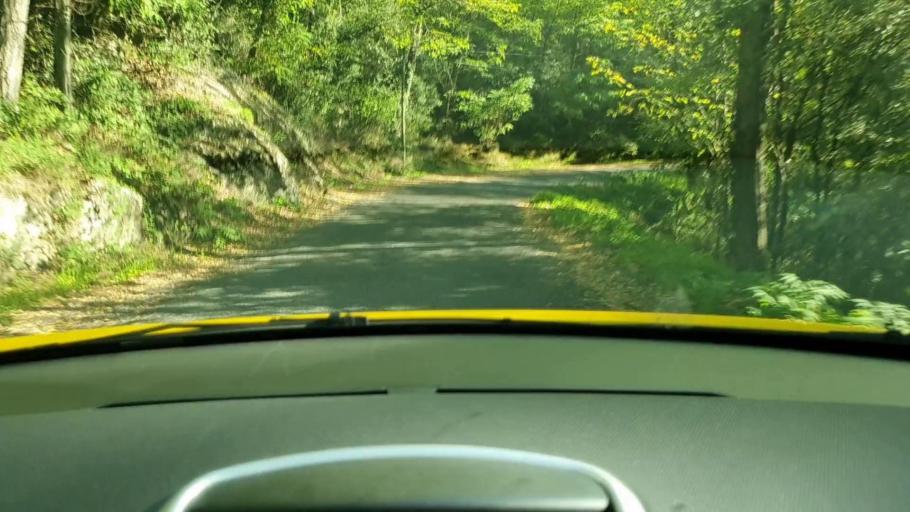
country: FR
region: Languedoc-Roussillon
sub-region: Departement du Gard
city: Valleraugue
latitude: 44.0382
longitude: 3.6788
